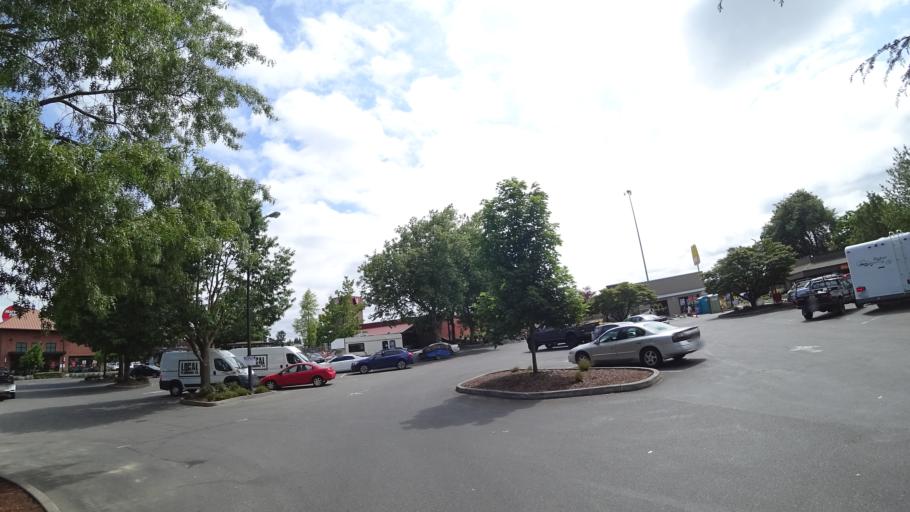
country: US
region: Washington
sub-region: Clark County
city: Vancouver
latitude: 45.6104
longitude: -122.6813
